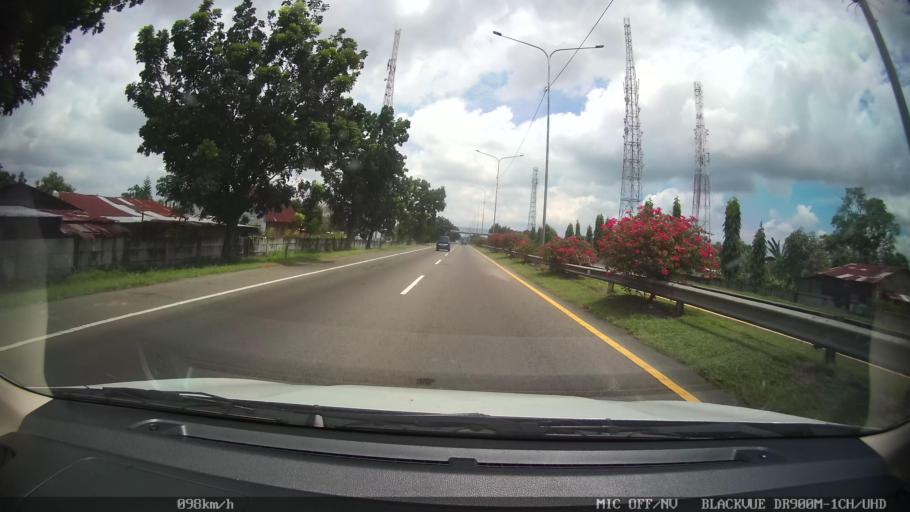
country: ID
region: North Sumatra
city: Medan
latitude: 3.6131
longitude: 98.7215
